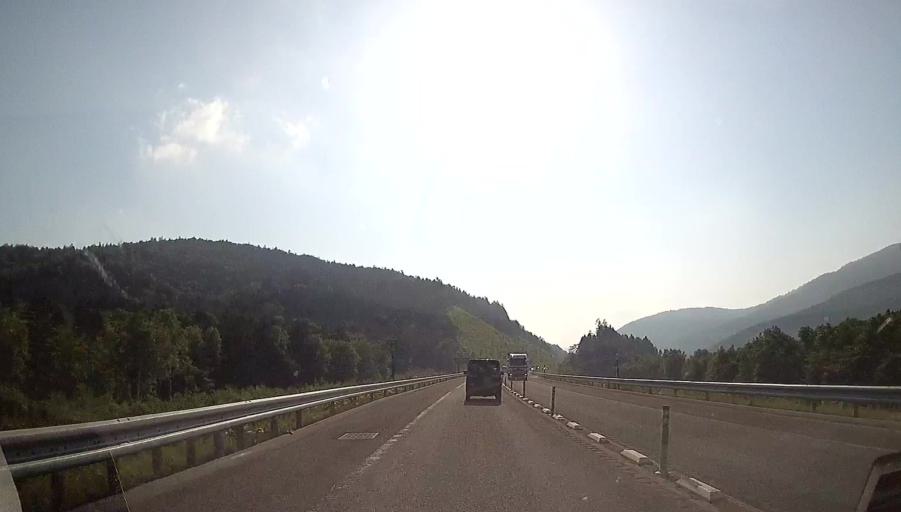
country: JP
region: Hokkaido
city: Shimo-furano
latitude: 43.0517
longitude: 142.6266
